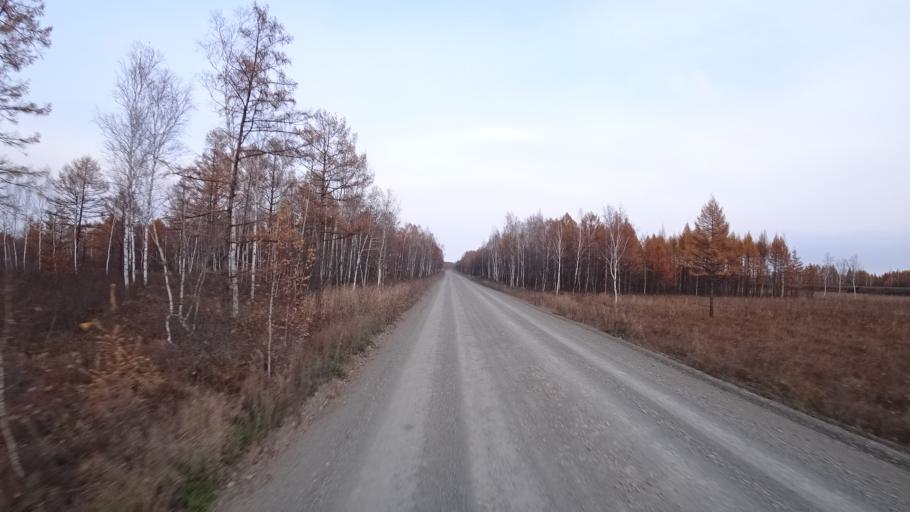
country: RU
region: Khabarovsk Krai
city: Amursk
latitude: 50.0108
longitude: 136.3994
